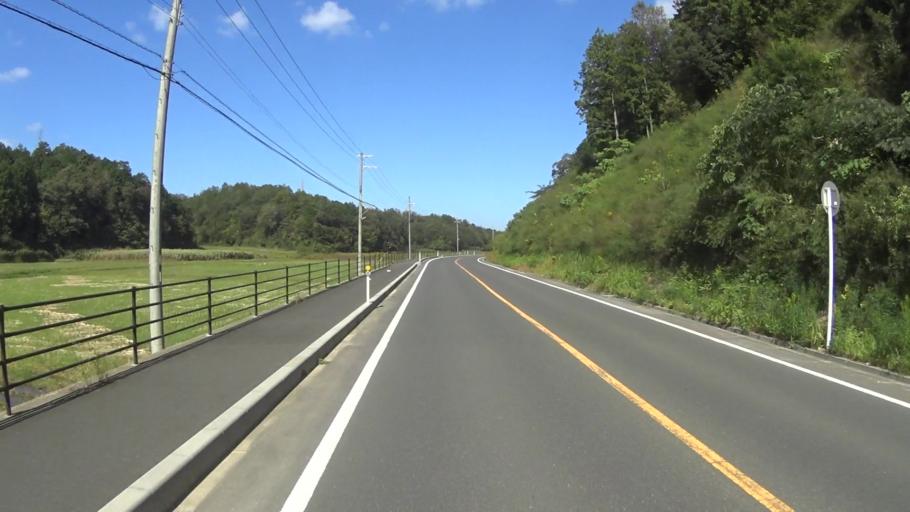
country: JP
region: Kyoto
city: Miyazu
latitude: 35.6434
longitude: 135.0716
